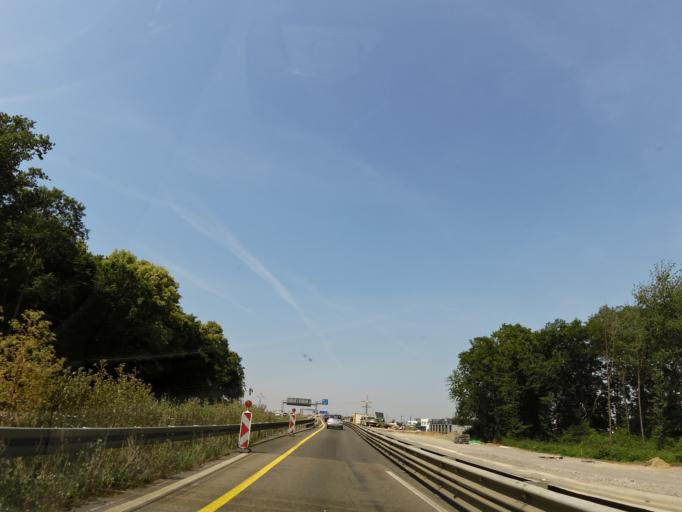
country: DE
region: North Rhine-Westphalia
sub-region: Regierungsbezirk Koln
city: Kerpen
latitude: 50.8912
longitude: 6.6618
